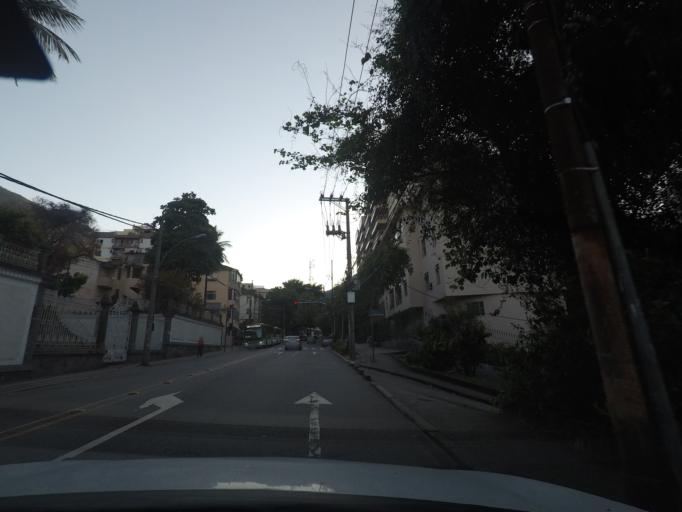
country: BR
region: Rio de Janeiro
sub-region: Rio De Janeiro
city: Rio de Janeiro
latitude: -22.9399
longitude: -43.2490
